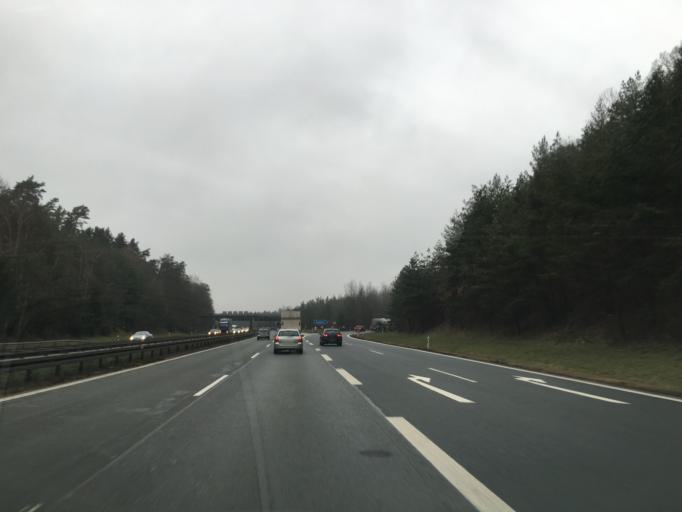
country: DE
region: Bavaria
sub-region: Regierungsbezirk Mittelfranken
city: Wendelstein
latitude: 49.3896
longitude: 11.1198
